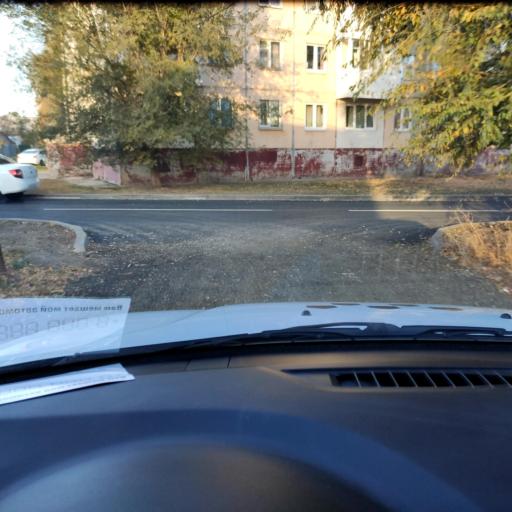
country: RU
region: Samara
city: Tol'yatti
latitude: 53.5308
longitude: 49.4225
